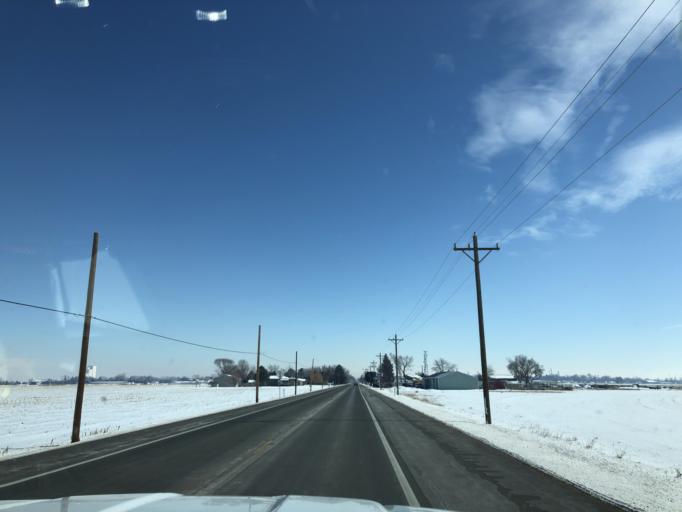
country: US
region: Colorado
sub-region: Morgan County
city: Fort Morgan
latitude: 40.2541
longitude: -103.8287
